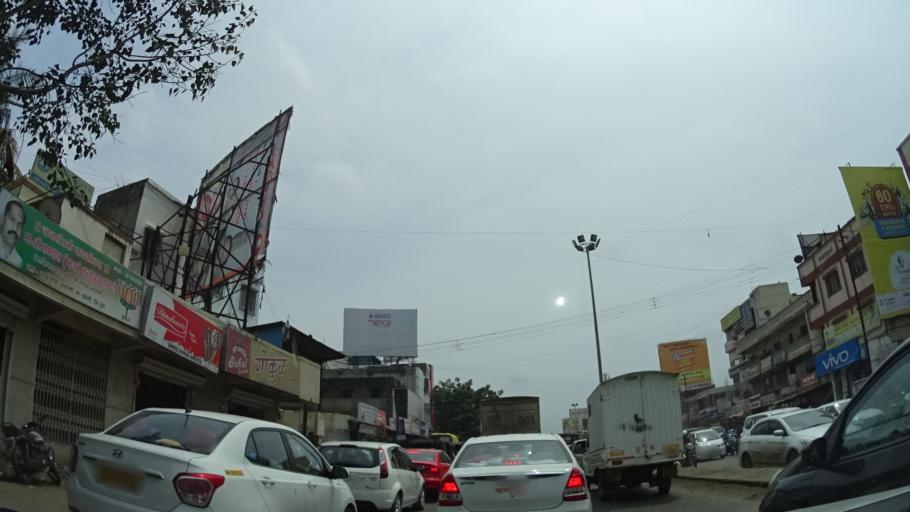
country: IN
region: Maharashtra
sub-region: Pune Division
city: Lohogaon
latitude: 18.5808
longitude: 73.9814
